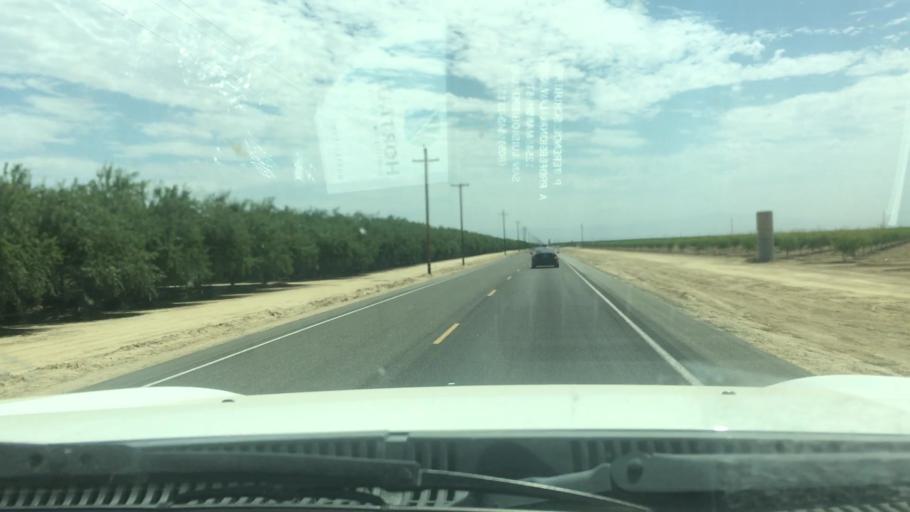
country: US
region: California
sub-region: Kern County
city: Wasco
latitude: 35.5580
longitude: -119.3093
